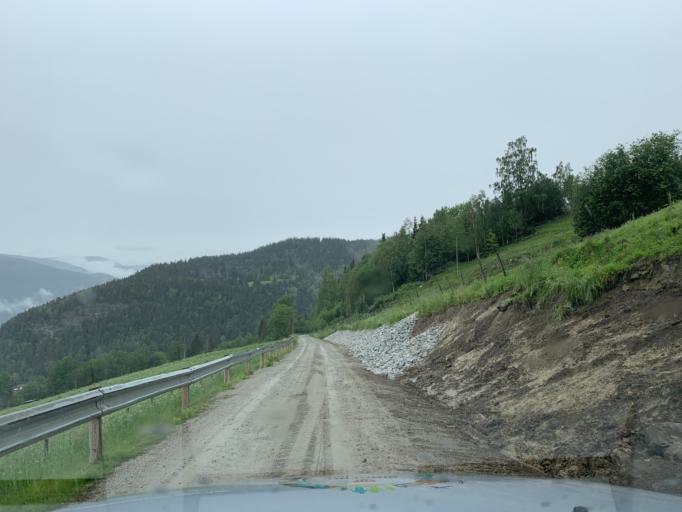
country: NO
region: Oppland
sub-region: Oyer
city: Tretten
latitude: 61.3867
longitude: 10.2828
